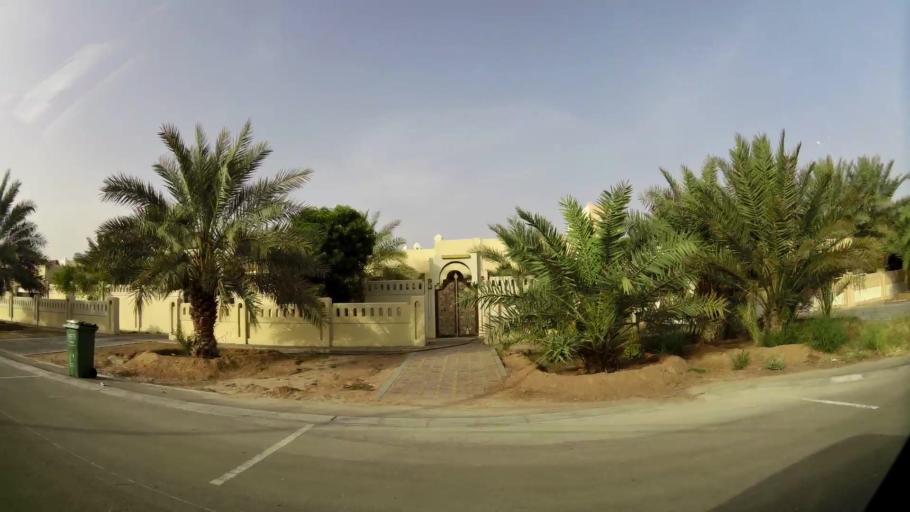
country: AE
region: Abu Dhabi
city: Al Ain
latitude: 24.1133
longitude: 55.7059
